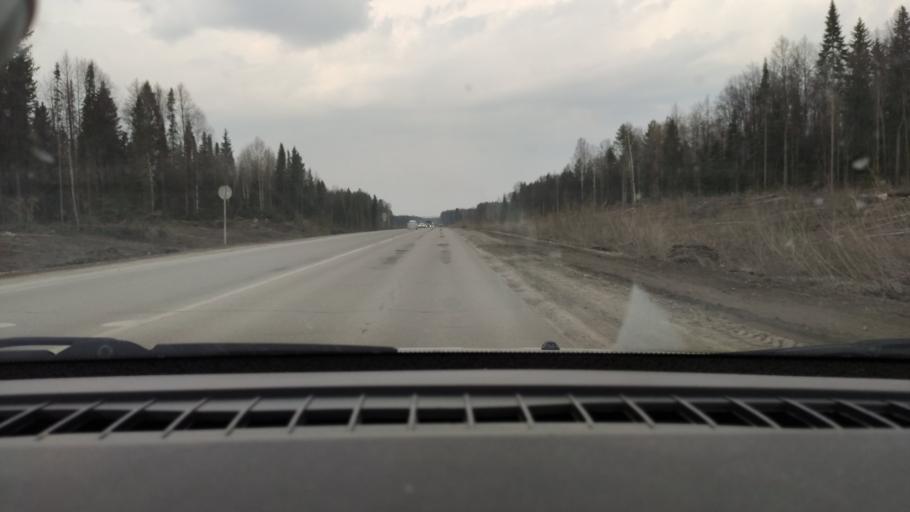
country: RU
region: Perm
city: Polazna
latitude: 58.1175
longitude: 56.4256
